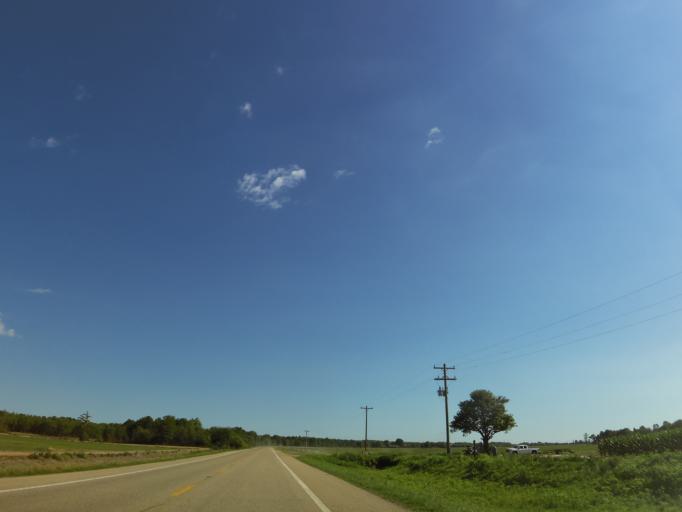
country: US
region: Arkansas
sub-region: Clay County
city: Corning
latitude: 36.4222
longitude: -90.4737
